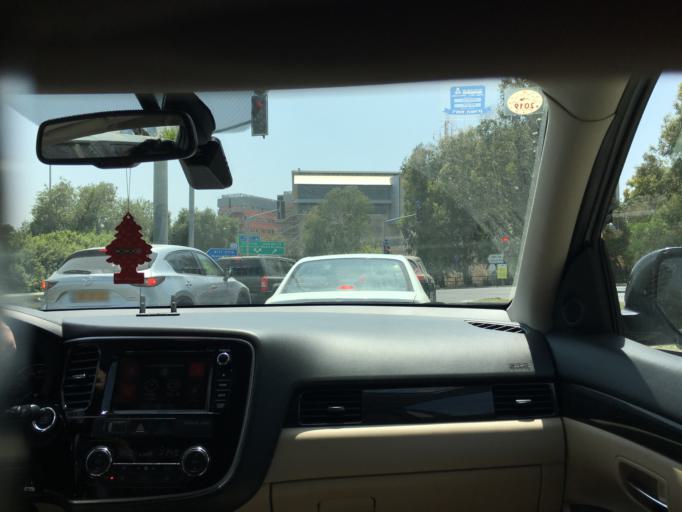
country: IL
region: Tel Aviv
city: Ramat Gan
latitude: 32.1037
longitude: 34.8036
